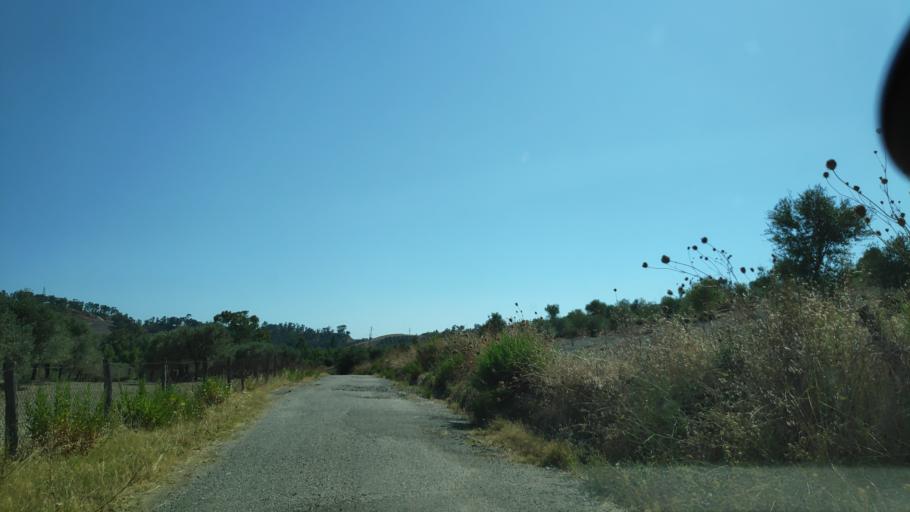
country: IT
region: Calabria
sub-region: Provincia di Reggio Calabria
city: Monasterace
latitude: 38.4305
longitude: 16.5247
